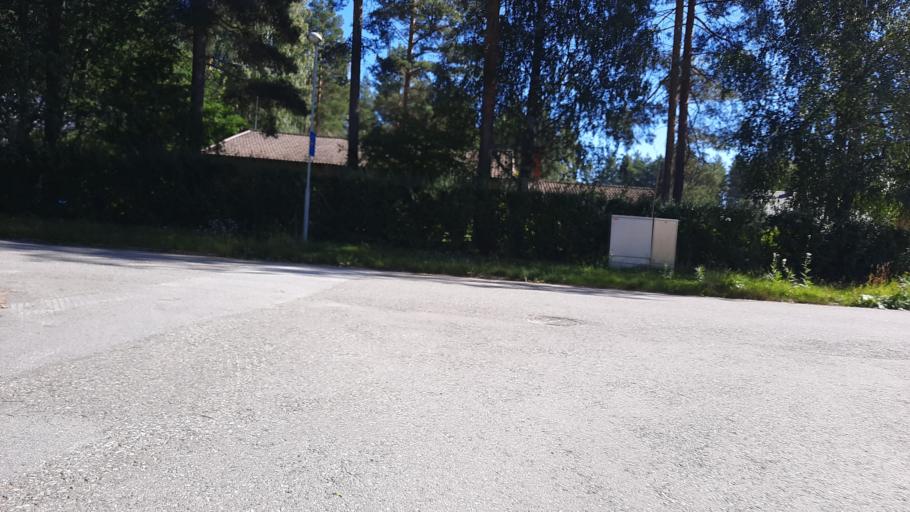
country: FI
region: North Karelia
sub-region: Joensuu
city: Joensuu
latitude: 62.6225
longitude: 29.7333
